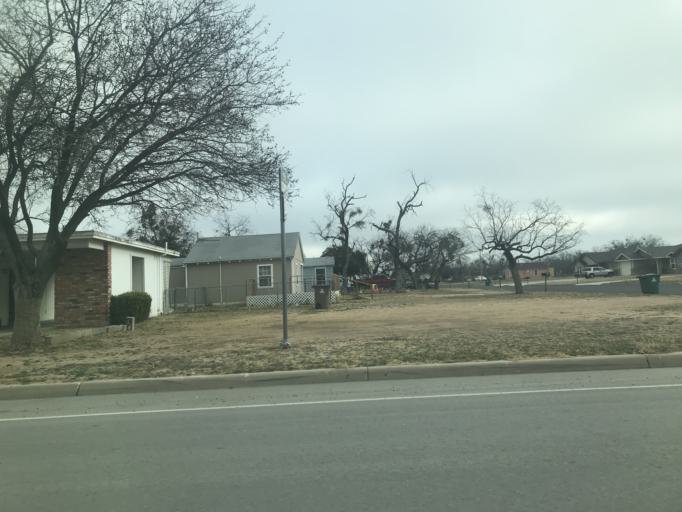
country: US
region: Texas
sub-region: Tom Green County
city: San Angelo
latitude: 31.4750
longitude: -100.4499
